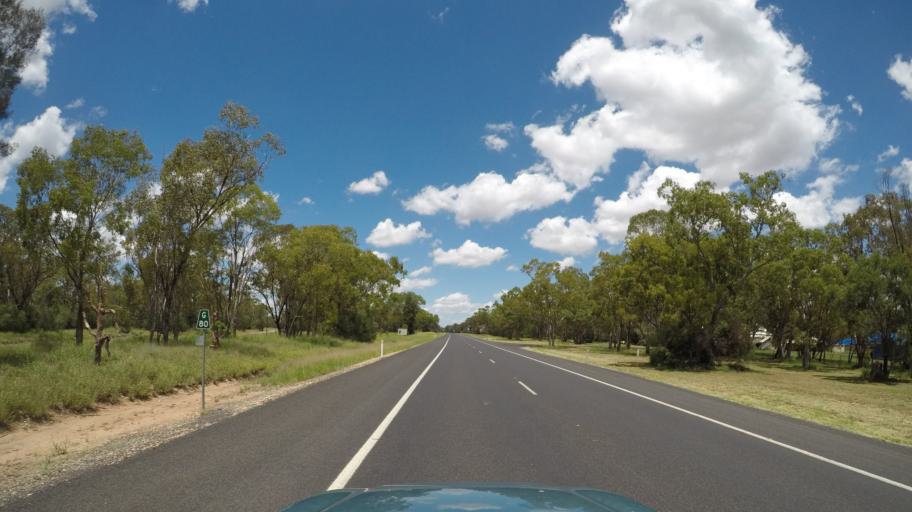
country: AU
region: Queensland
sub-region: Goondiwindi
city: Goondiwindi
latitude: -28.0796
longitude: 150.7408
